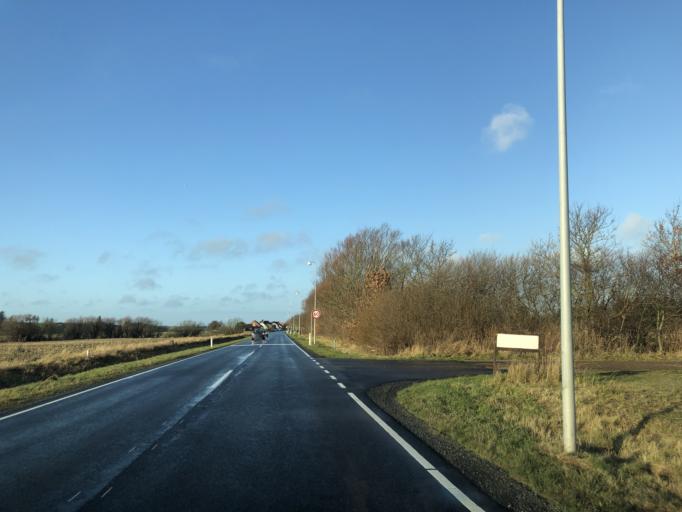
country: DK
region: Central Jutland
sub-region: Struer Kommune
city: Struer
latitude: 56.5471
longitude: 8.4931
